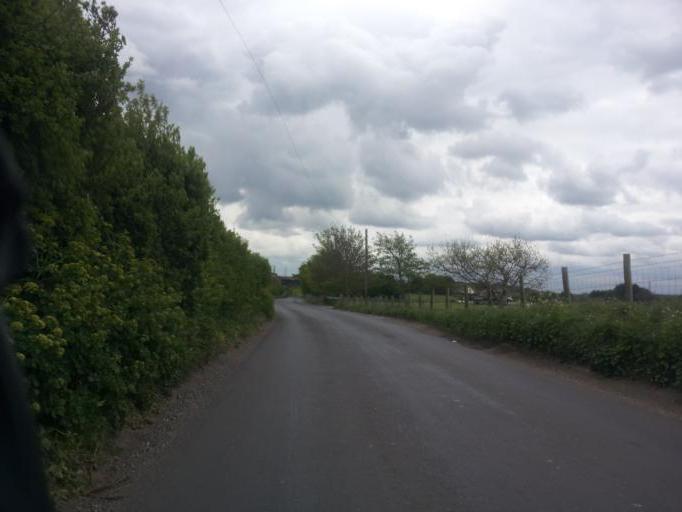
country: GB
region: England
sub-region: Kent
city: Newington
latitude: 51.3755
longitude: 0.6612
